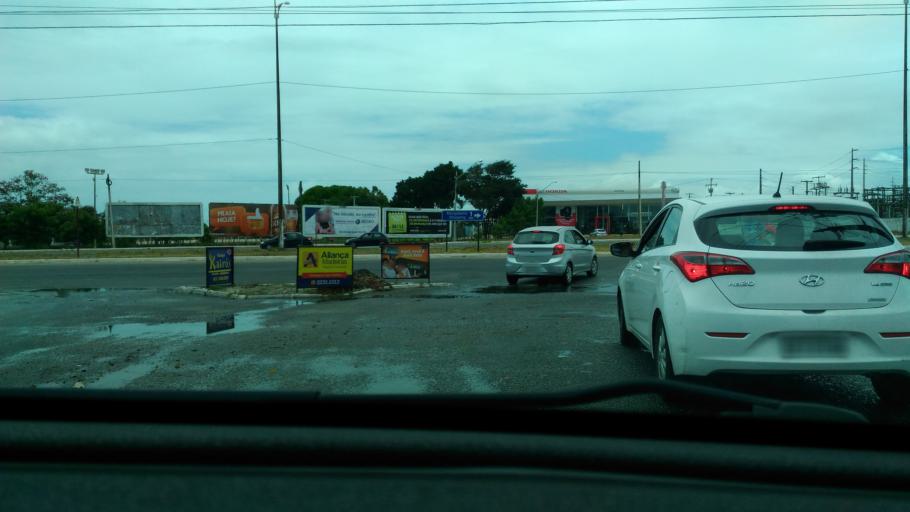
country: BR
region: Paraiba
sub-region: Joao Pessoa
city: Joao Pessoa
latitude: -7.1601
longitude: -34.8190
